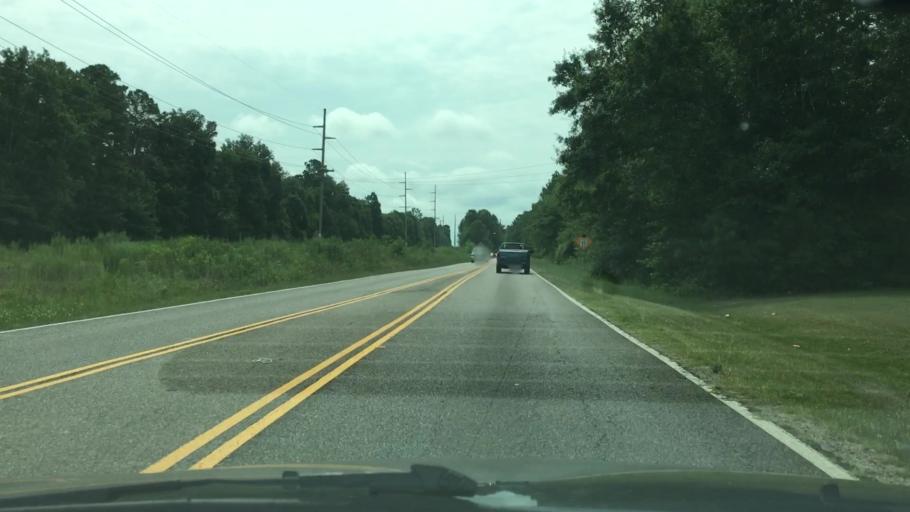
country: US
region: South Carolina
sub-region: Aiken County
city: Aiken
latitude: 33.5244
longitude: -81.7333
